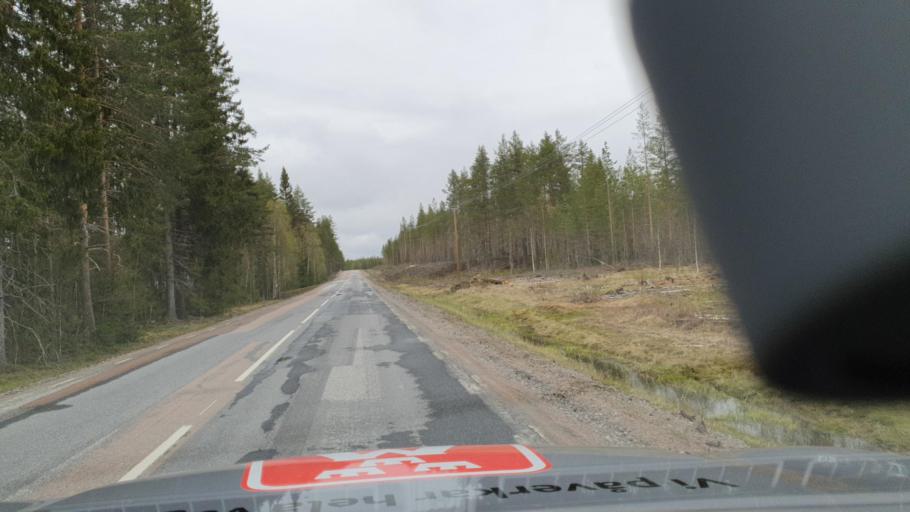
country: SE
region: Vaesternorrland
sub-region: Solleftea Kommun
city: Solleftea
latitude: 63.6359
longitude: 17.4215
